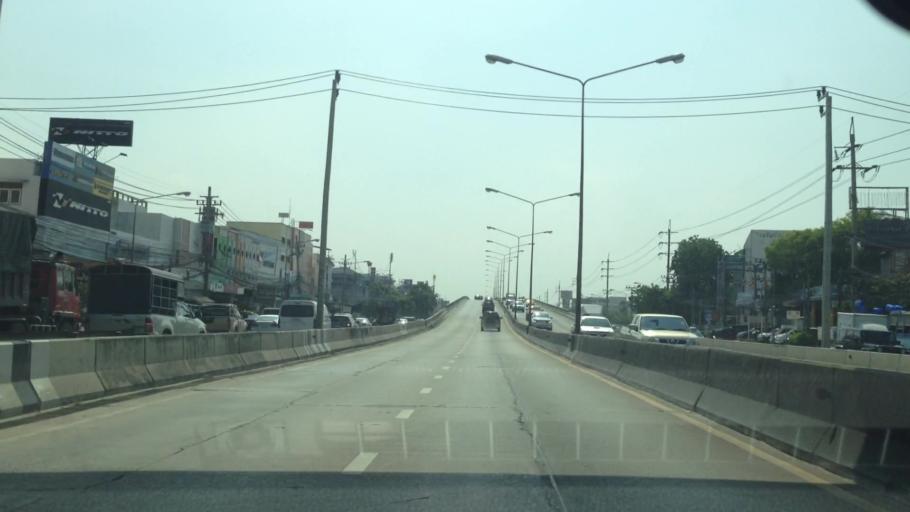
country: TH
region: Bangkok
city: Sai Mai
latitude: 13.9491
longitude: 100.6226
